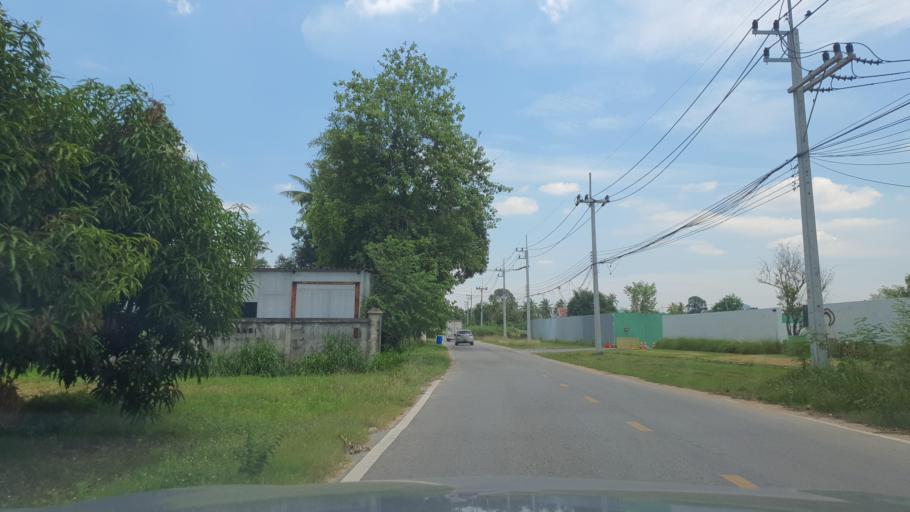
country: TH
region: Chon Buri
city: Phatthaya
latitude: 12.8104
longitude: 100.9439
